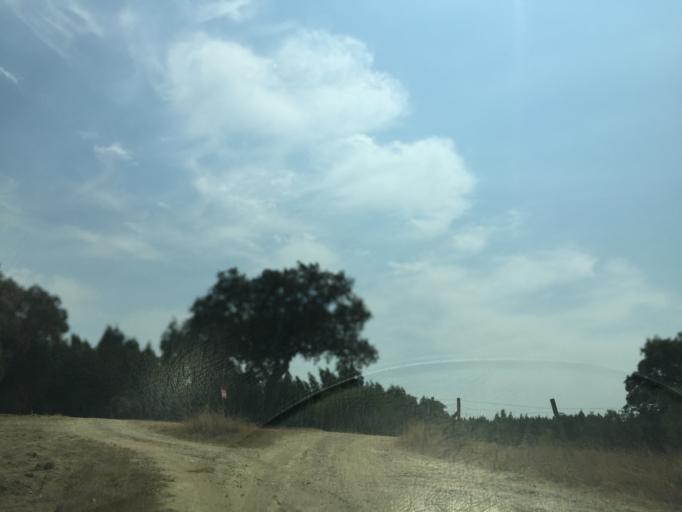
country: PT
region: Setubal
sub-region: Grandola
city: Grandola
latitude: 38.0436
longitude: -8.4773
